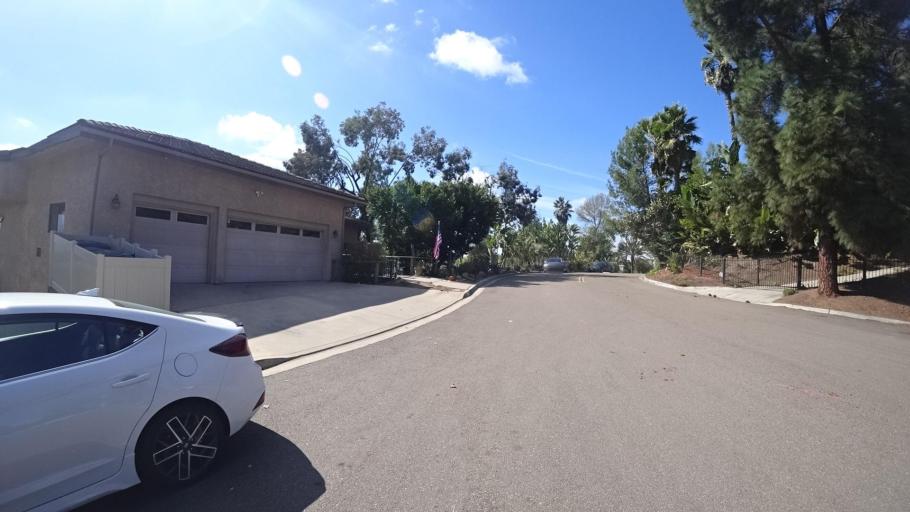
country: US
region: California
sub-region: San Diego County
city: Rancho San Diego
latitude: 32.7663
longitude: -116.9330
